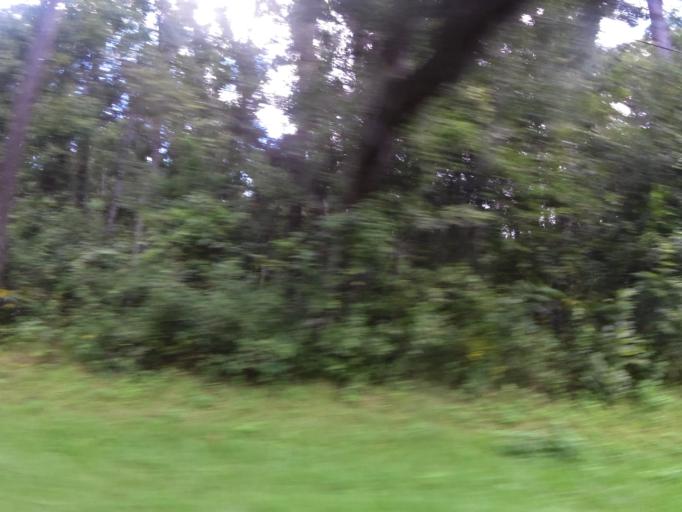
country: US
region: Florida
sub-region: Putnam County
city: East Palatka
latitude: 29.7785
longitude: -81.4863
